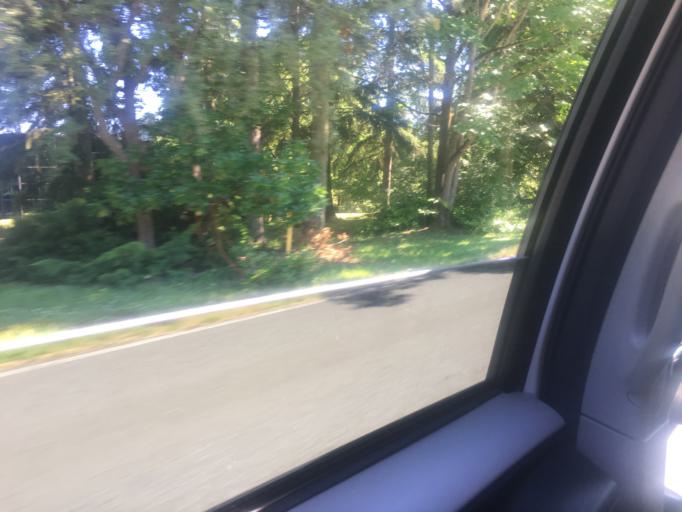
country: US
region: Washington
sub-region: King County
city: Bellevue
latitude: 47.6101
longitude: -122.1793
